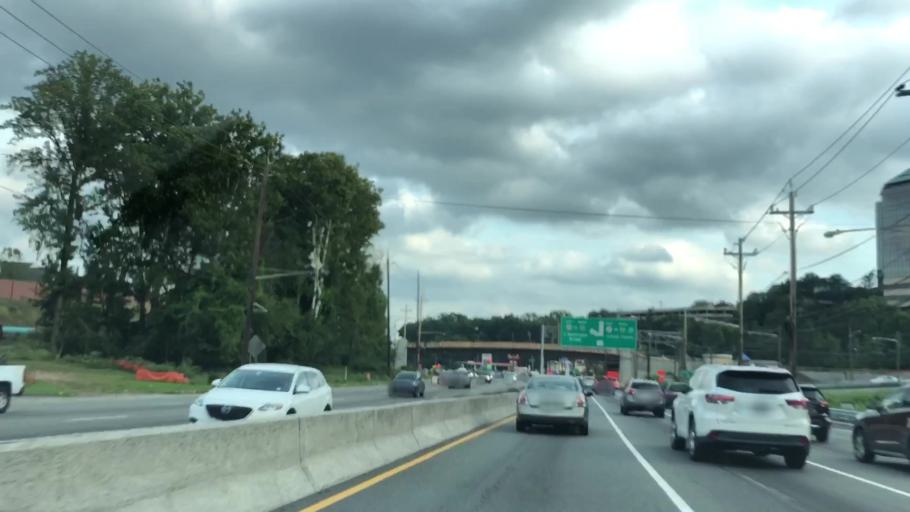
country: US
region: New Jersey
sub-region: Passaic County
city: Little Falls
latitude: 40.8743
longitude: -74.1978
